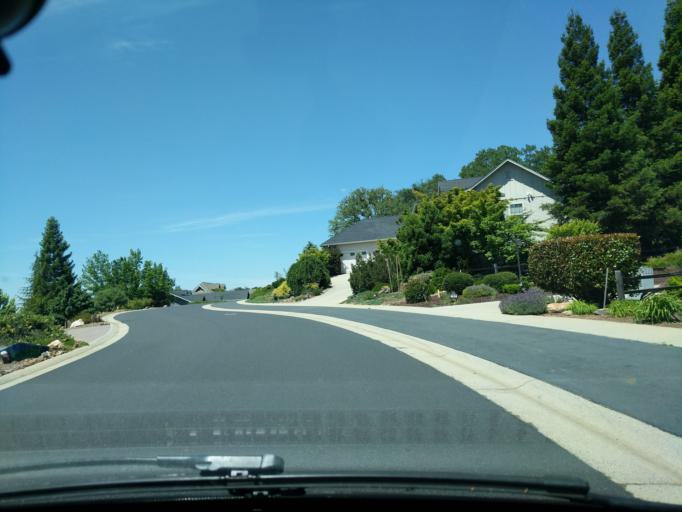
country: US
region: California
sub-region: Calaveras County
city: Angels Camp
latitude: 38.0721
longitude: -120.5592
